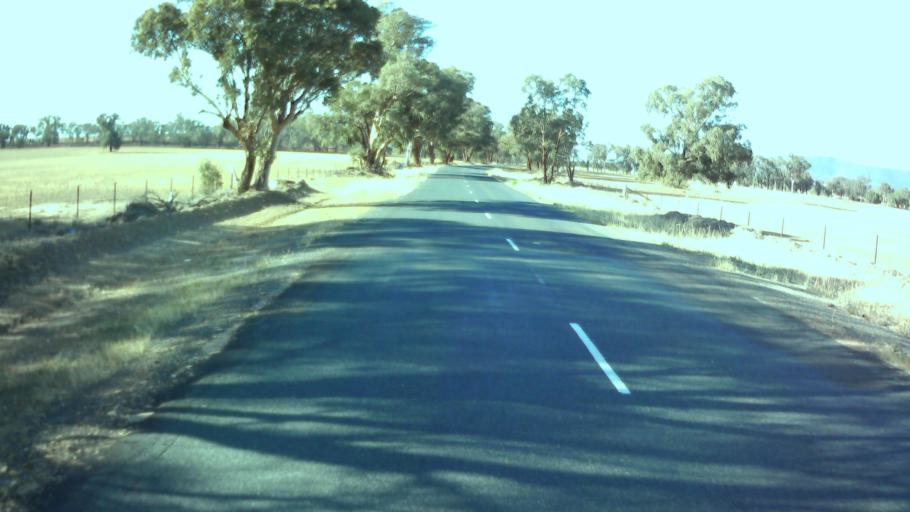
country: AU
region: New South Wales
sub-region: Weddin
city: Grenfell
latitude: -33.9373
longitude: 148.1374
